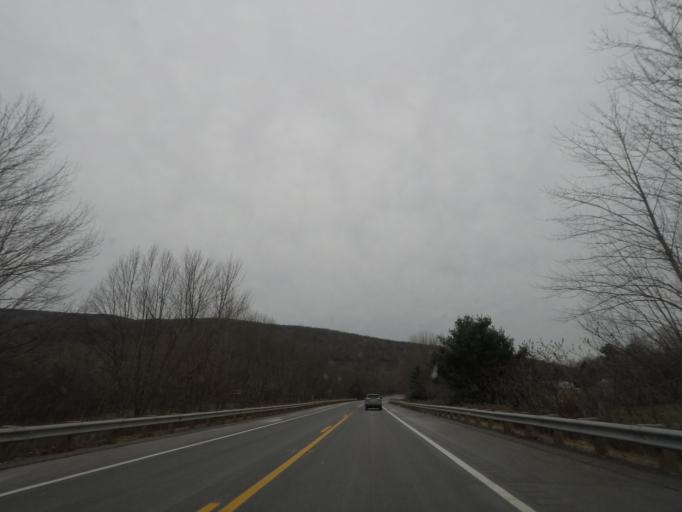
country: US
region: Massachusetts
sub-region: Berkshire County
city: Lanesborough
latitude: 42.5453
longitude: -73.3141
